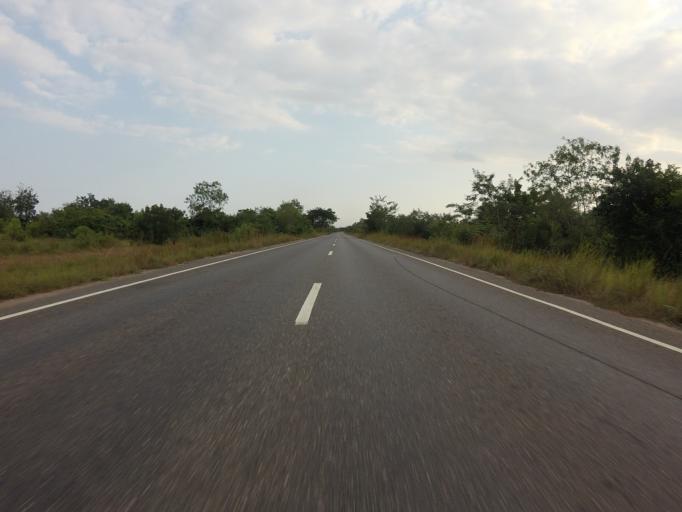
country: GH
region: Volta
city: Ho
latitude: 6.1255
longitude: 0.5221
